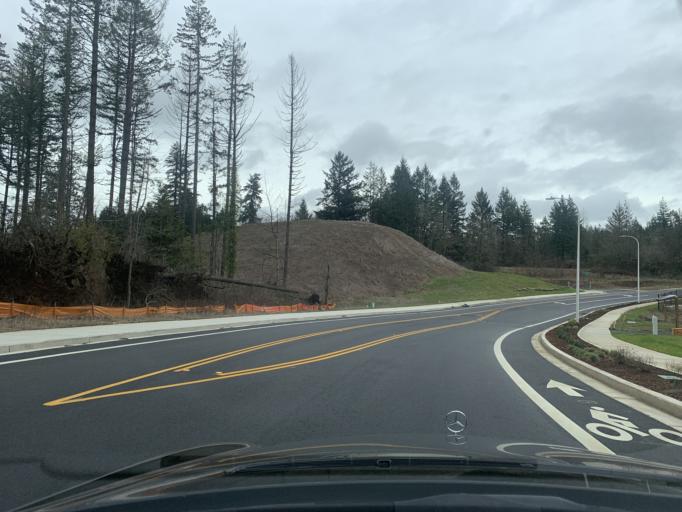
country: US
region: Oregon
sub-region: Clackamas County
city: Happy Valley
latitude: 45.4455
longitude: -122.5040
